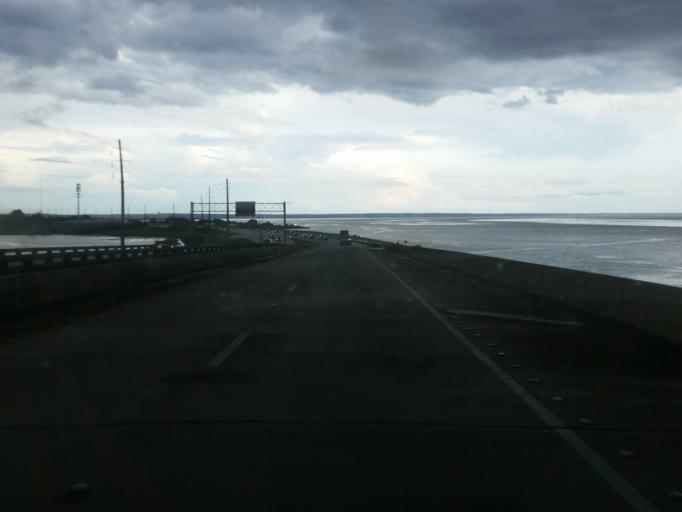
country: US
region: Alabama
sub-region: Mobile County
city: Mobile
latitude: 30.6832
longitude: -88.0081
